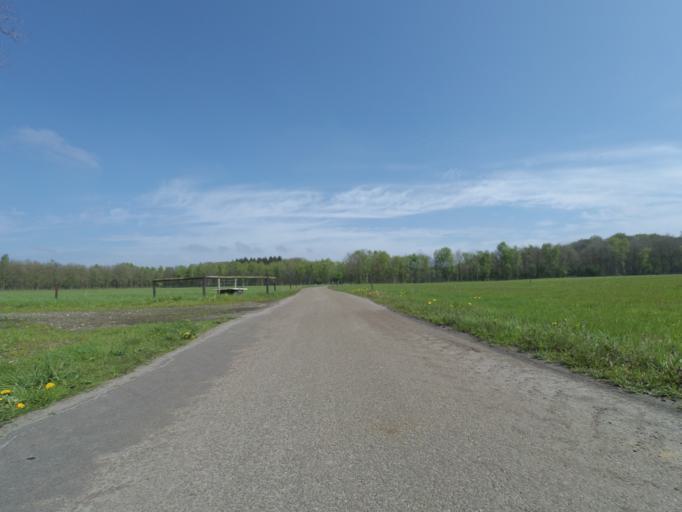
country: NL
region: Gelderland
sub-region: Gemeente Barneveld
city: Garderen
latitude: 52.2962
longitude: 5.7121
